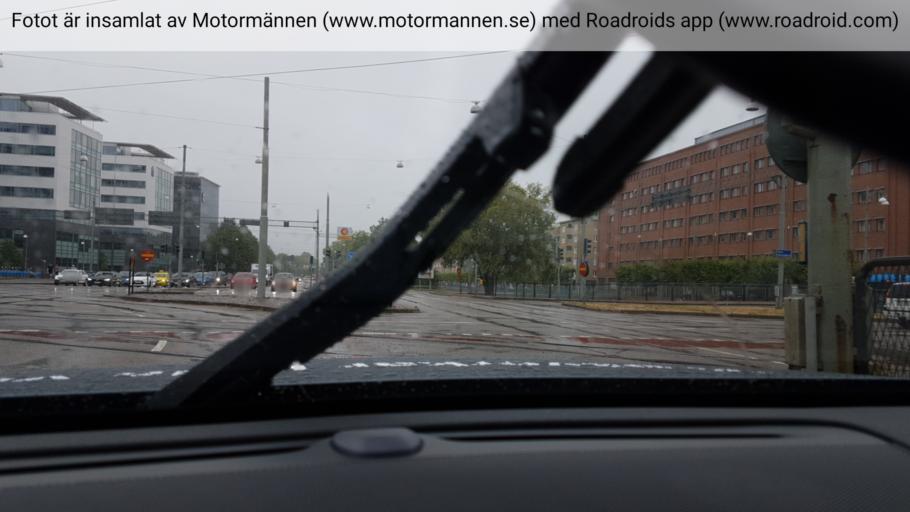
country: SE
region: Vaestra Goetaland
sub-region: Goteborg
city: Goeteborg
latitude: 57.7066
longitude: 11.9859
